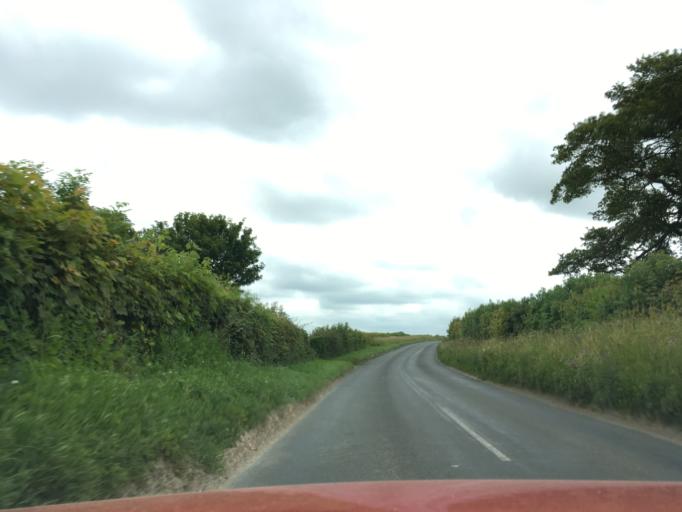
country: GB
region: England
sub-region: Oxfordshire
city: Chipping Norton
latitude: 51.9234
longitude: -1.5823
